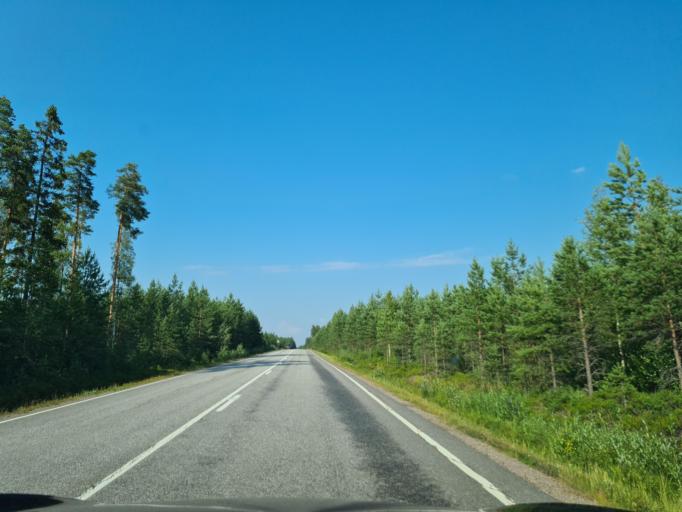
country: FI
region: Satakunta
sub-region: Pohjois-Satakunta
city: Karvia
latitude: 62.2940
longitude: 22.6210
